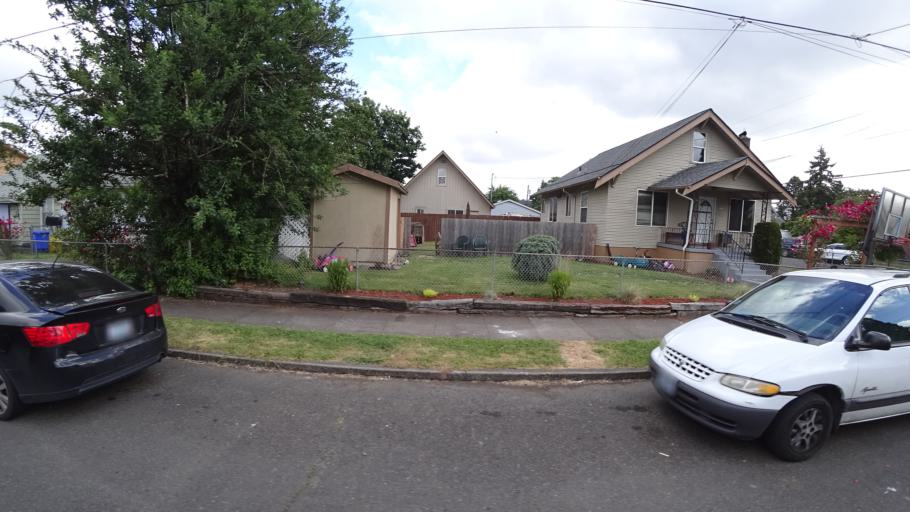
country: US
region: Oregon
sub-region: Multnomah County
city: Lents
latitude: 45.4806
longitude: -122.5639
